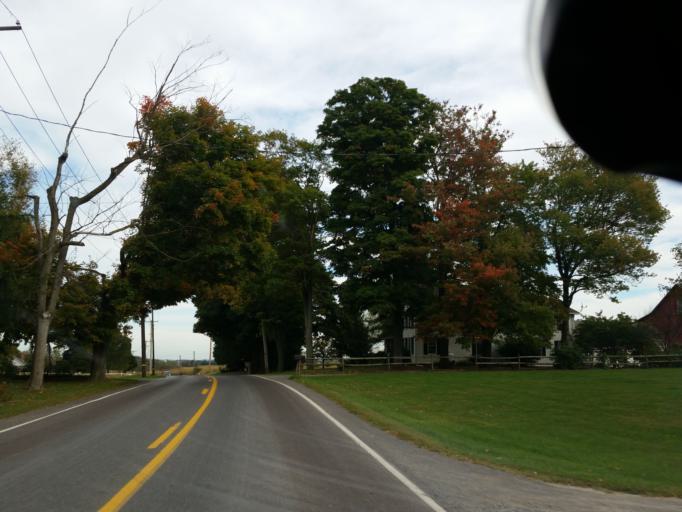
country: US
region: Pennsylvania
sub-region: Lycoming County
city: South Williamsport
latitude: 41.1227
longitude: -76.9871
